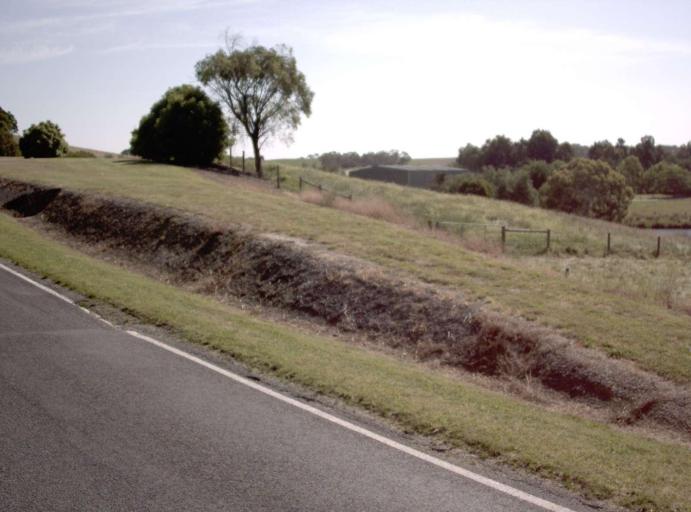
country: AU
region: Victoria
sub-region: Baw Baw
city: Warragul
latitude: -38.3176
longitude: 145.7718
